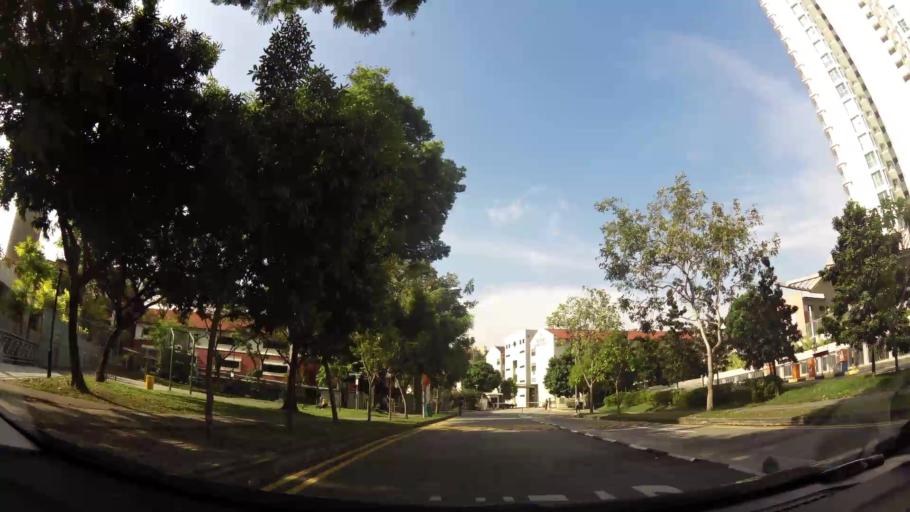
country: SG
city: Singapore
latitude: 1.3558
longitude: 103.8441
